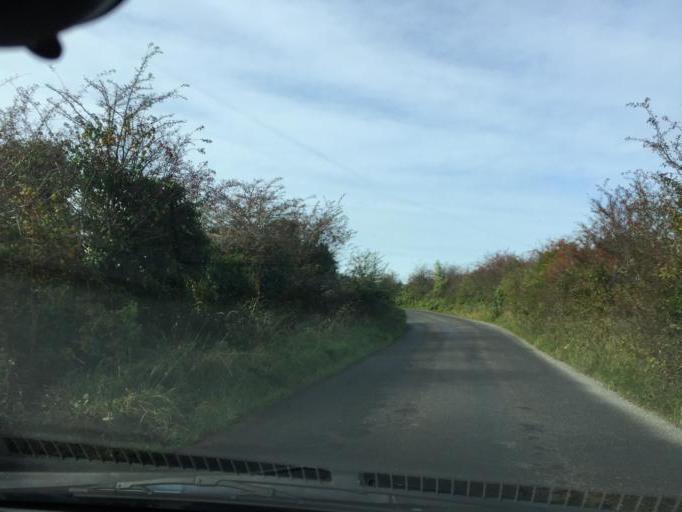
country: IE
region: Connaught
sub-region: Roscommon
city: Boyle
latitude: 54.0553
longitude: -8.2490
